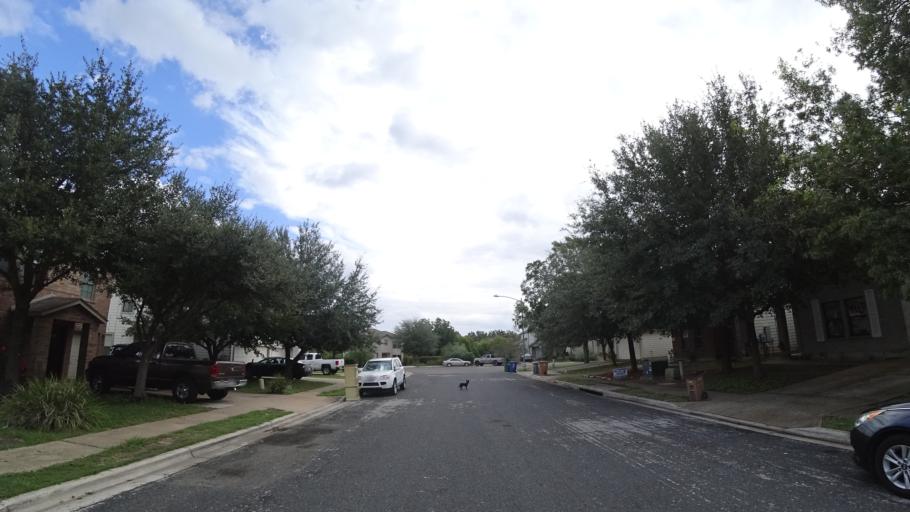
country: US
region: Texas
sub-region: Travis County
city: Onion Creek
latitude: 30.1516
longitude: -97.7379
